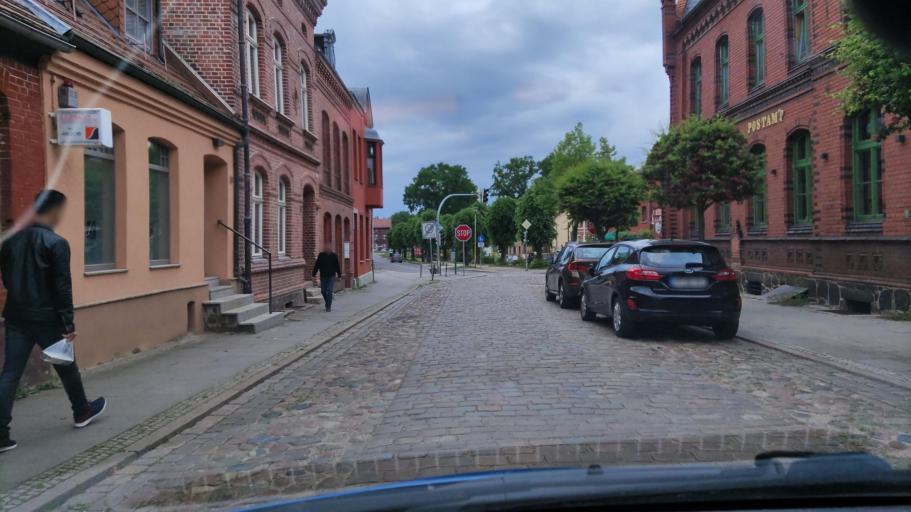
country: DE
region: Mecklenburg-Vorpommern
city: Plau am See
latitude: 53.4590
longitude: 12.2597
